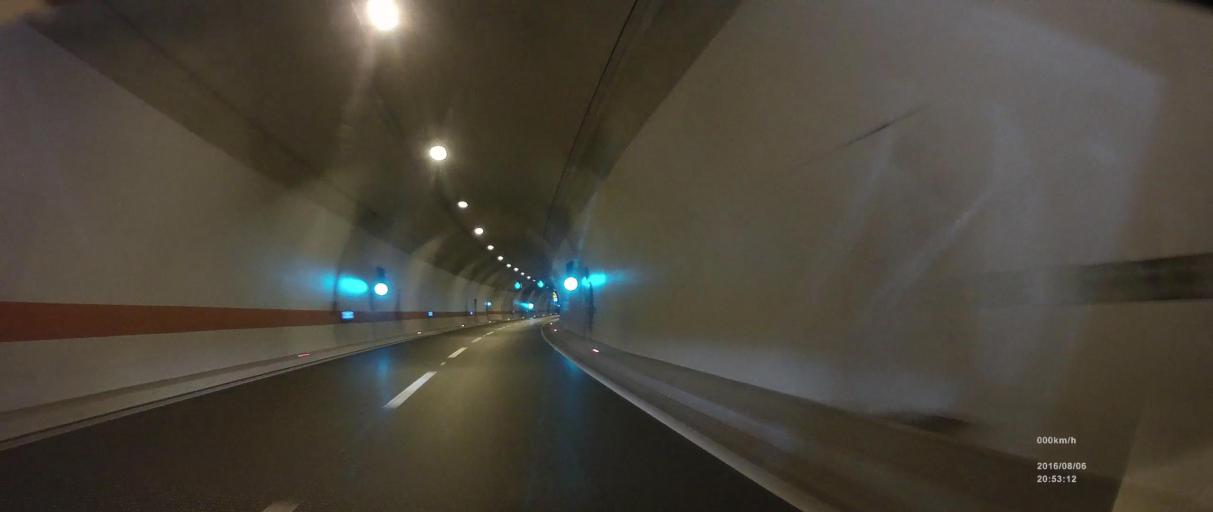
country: BA
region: Federation of Bosnia and Herzegovina
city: Ljubuski
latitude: 43.1401
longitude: 17.4848
